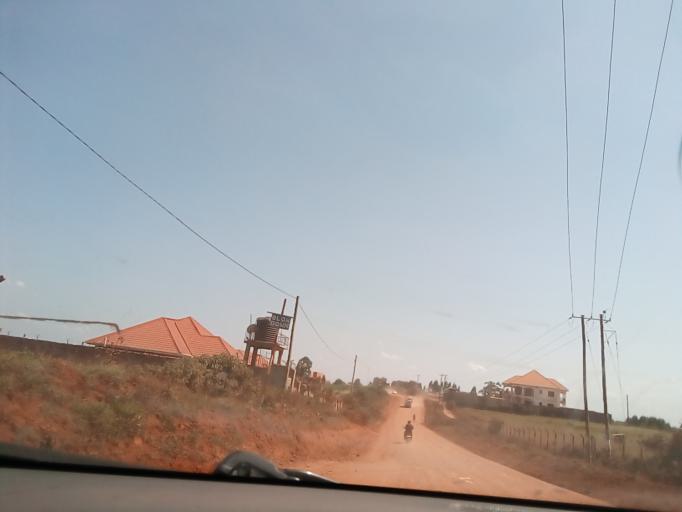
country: UG
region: Central Region
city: Masaka
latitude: -0.3638
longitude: 31.7487
